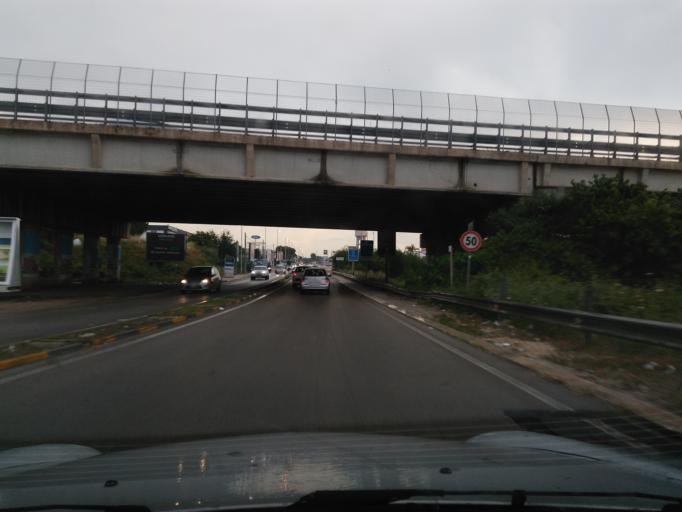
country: IT
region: Apulia
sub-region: Provincia di Bari
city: Molfetta
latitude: 41.2073
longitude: 16.5615
